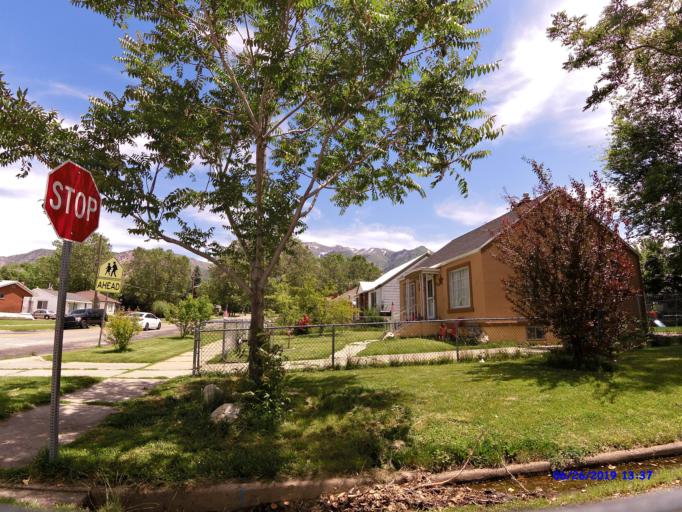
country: US
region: Utah
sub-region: Weber County
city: South Ogden
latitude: 41.2058
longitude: -111.9596
